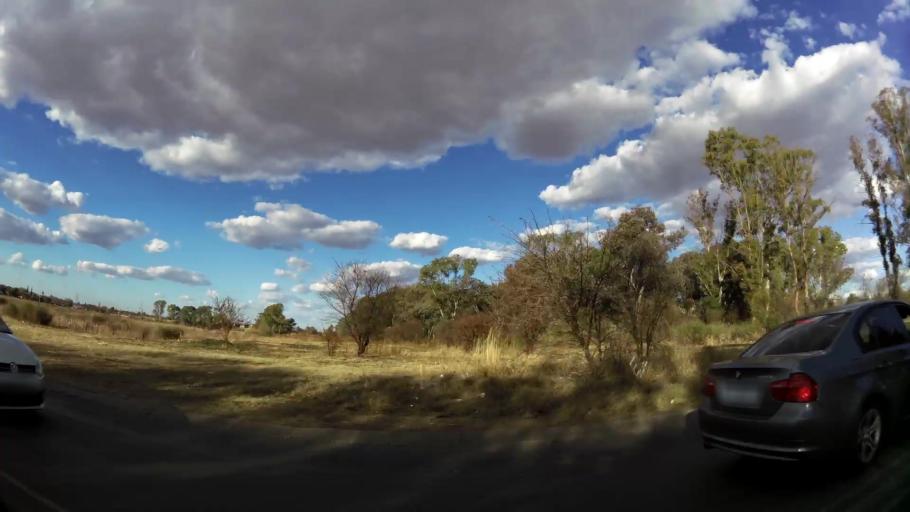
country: ZA
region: North-West
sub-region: Dr Kenneth Kaunda District Municipality
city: Potchefstroom
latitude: -26.7081
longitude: 27.0777
